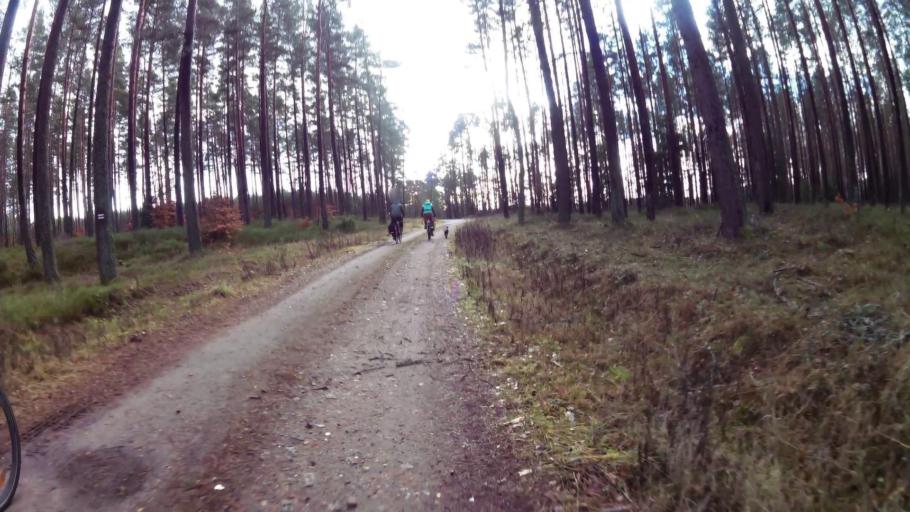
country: PL
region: West Pomeranian Voivodeship
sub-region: Powiat koszalinski
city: Sianow
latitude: 54.0804
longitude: 16.2905
